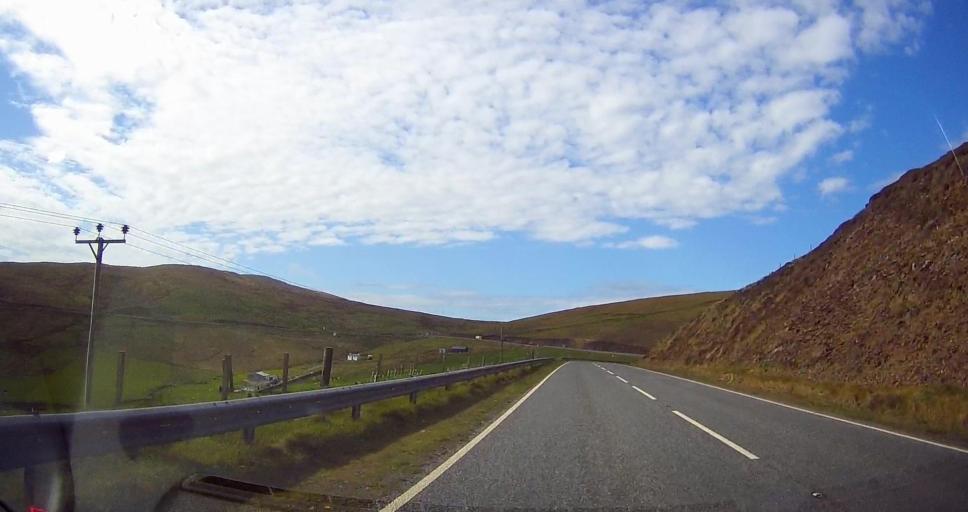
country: GB
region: Scotland
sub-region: Shetland Islands
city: Sandwick
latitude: 59.9924
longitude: -1.2794
